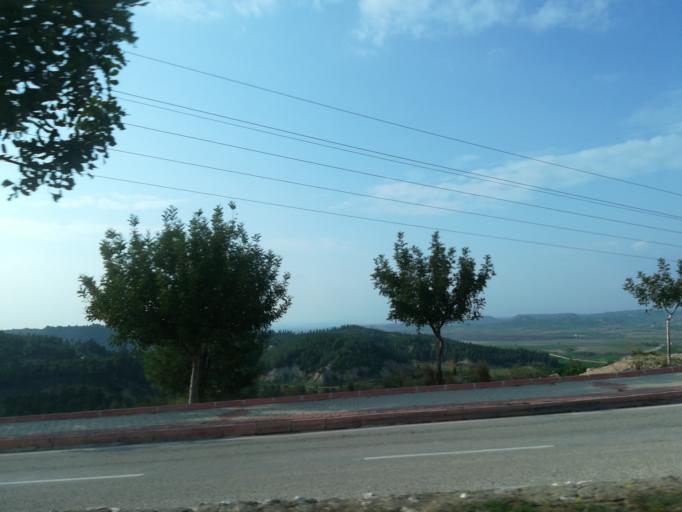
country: TR
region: Adana
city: Adana
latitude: 37.0689
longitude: 35.3781
